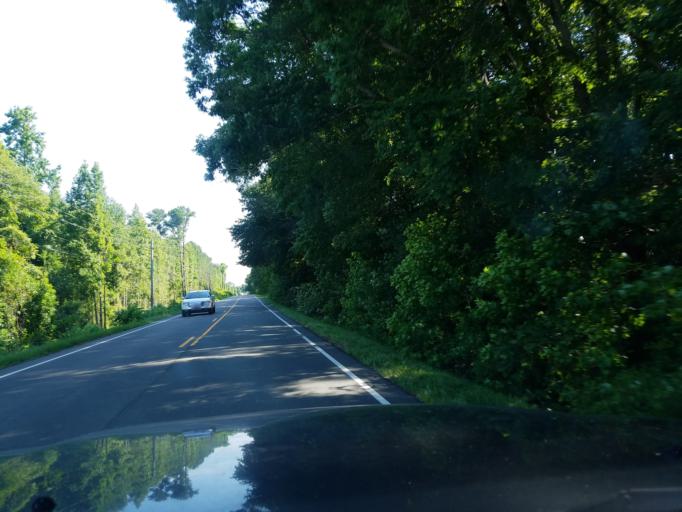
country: US
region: North Carolina
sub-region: Granville County
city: Butner
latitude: 36.2198
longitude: -78.7226
